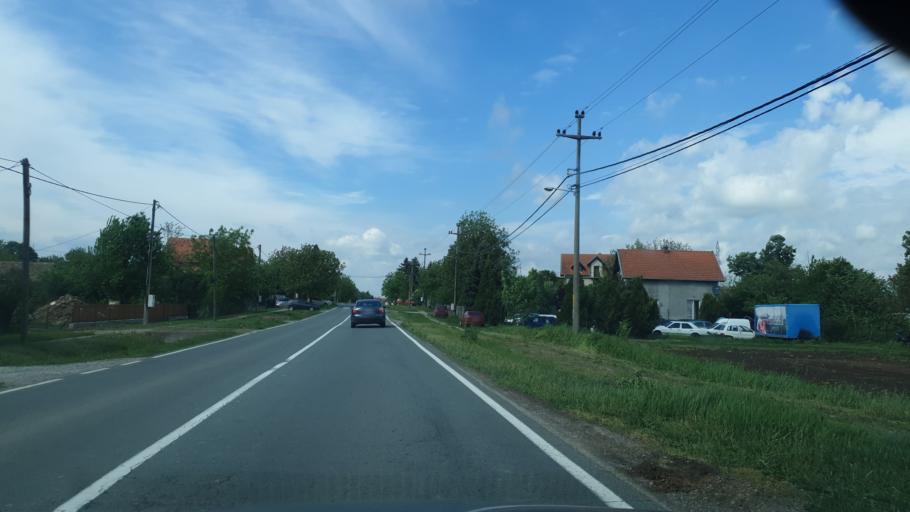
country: RS
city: Stubline
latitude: 44.5610
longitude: 20.1478
